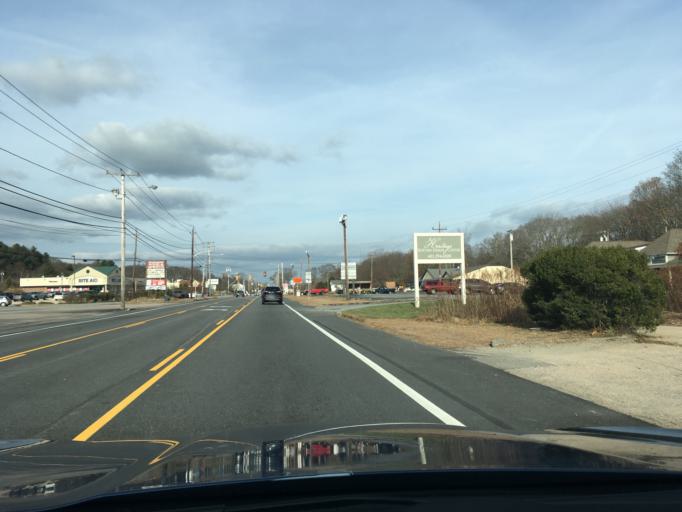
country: US
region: Rhode Island
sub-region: Washington County
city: North Kingstown
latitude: 41.5872
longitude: -71.4582
